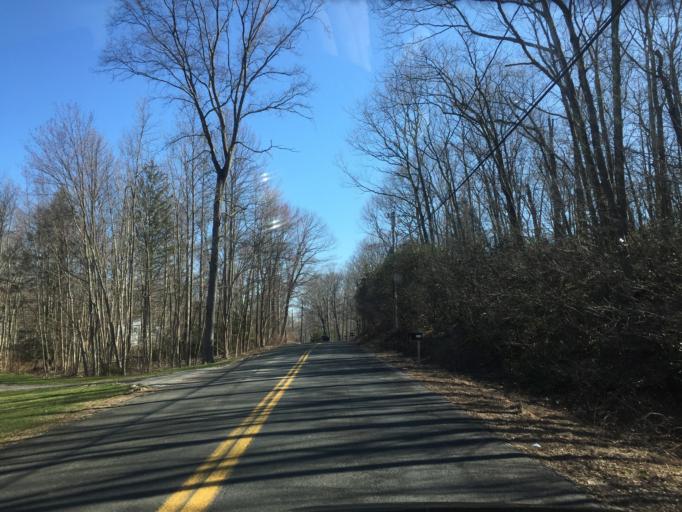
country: US
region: Connecticut
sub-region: Hartford County
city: Terramuggus
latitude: 41.6613
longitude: -72.4750
